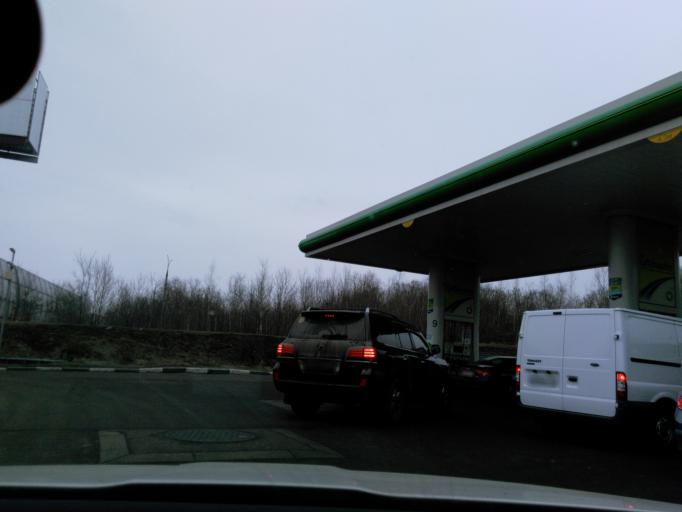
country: RU
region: Moscow
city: Novyye Cheremushki
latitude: 55.7016
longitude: 37.6053
